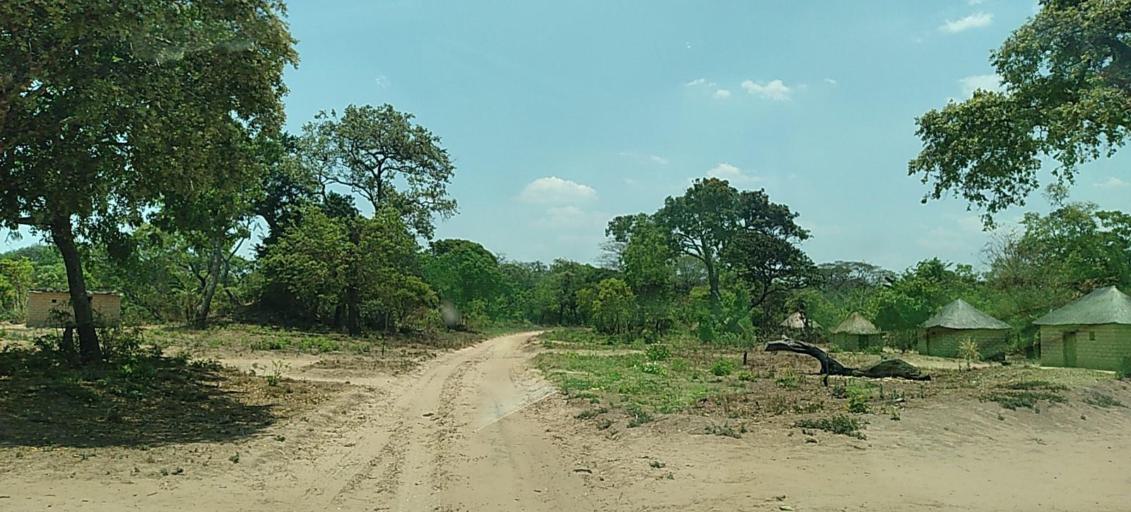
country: CD
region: Katanga
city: Kolwezi
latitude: -11.3655
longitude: 25.2081
